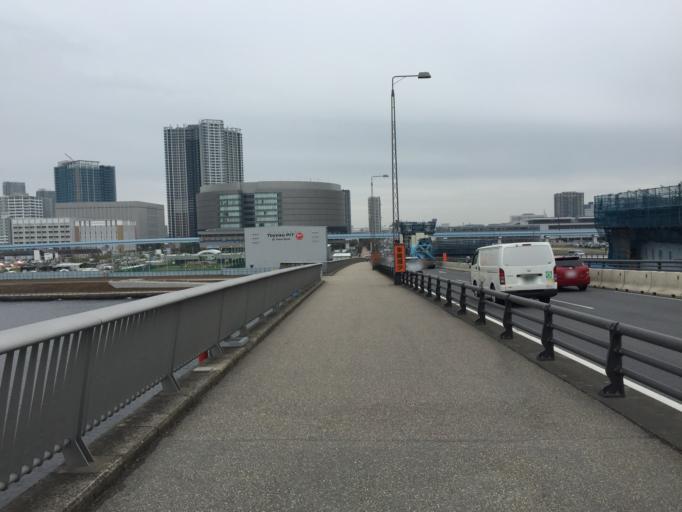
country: JP
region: Tokyo
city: Tokyo
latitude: 35.6514
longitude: 139.7861
